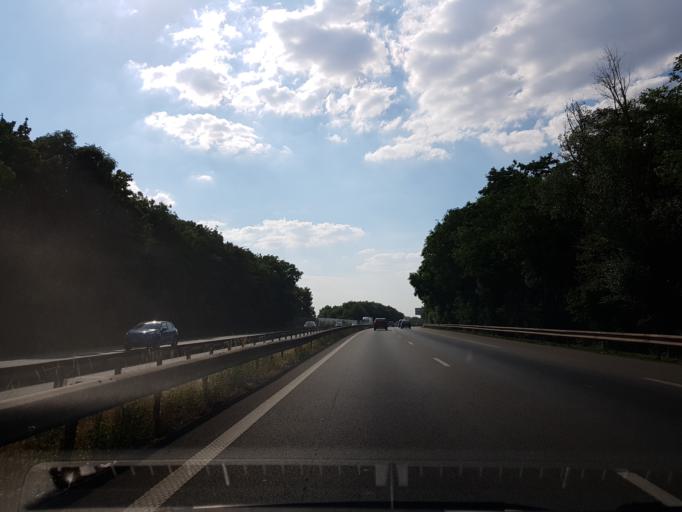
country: FR
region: Nord-Pas-de-Calais
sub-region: Departement du Pas-de-Calais
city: Courcelles-les-Lens
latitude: 50.4252
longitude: 3.0085
